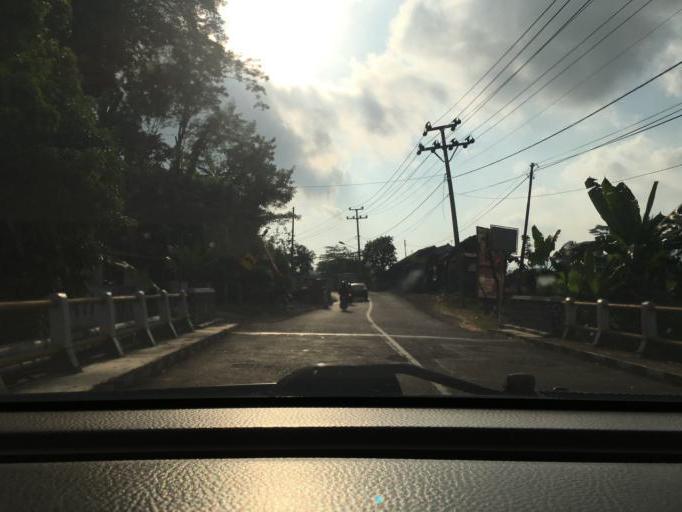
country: ID
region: West Java
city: Nusaherang
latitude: -7.0077
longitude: 108.4418
